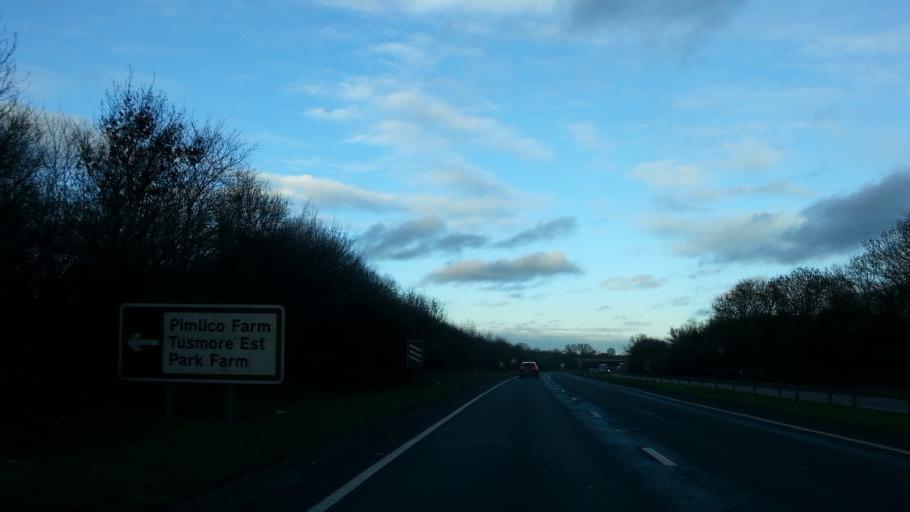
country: GB
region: England
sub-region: Northamptonshire
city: Brackley
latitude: 51.9696
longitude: -1.1946
